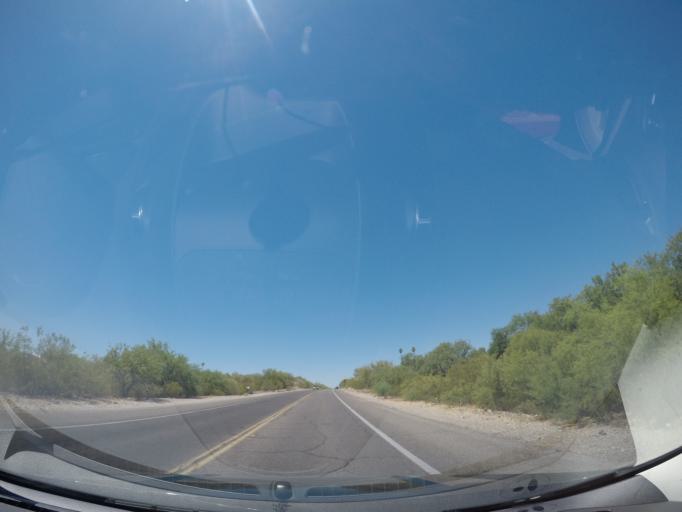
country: US
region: Arizona
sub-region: Pima County
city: Tanque Verde
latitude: 32.2805
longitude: -110.7689
